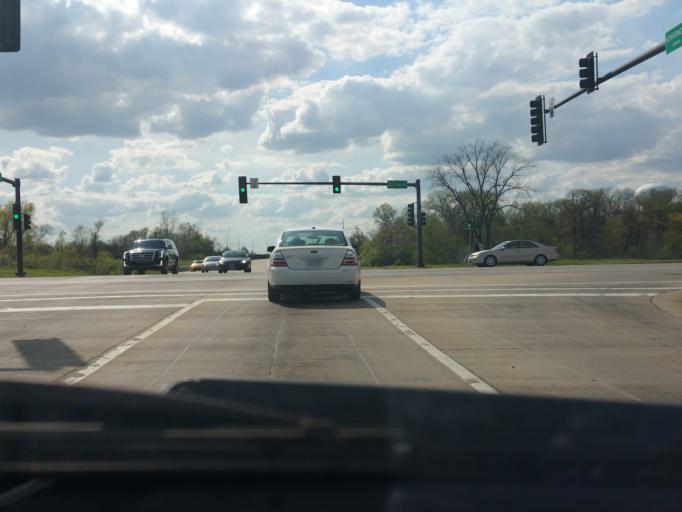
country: US
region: Illinois
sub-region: Madison County
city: Edwardsville
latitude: 38.7872
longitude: -89.9566
